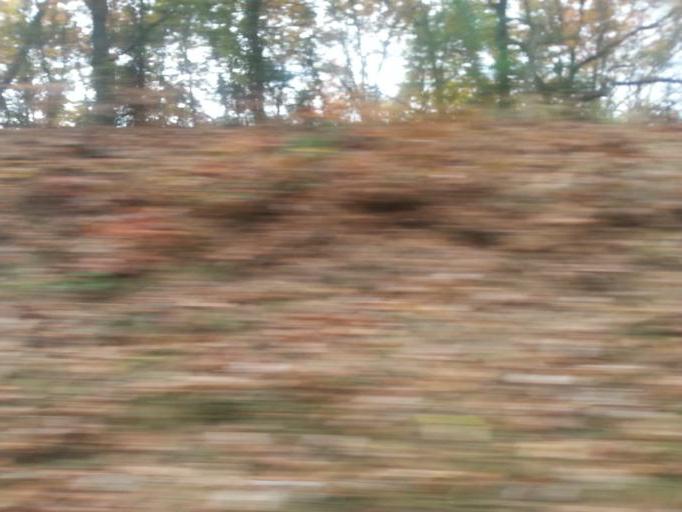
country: US
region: Virginia
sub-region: City of Galax
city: Galax
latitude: 36.5551
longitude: -80.9085
